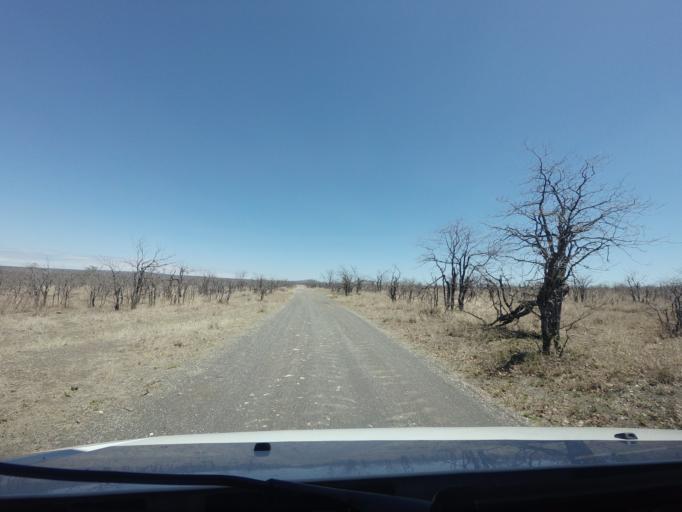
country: ZA
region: Limpopo
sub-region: Mopani District Municipality
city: Phalaborwa
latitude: -23.6389
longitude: 31.4866
